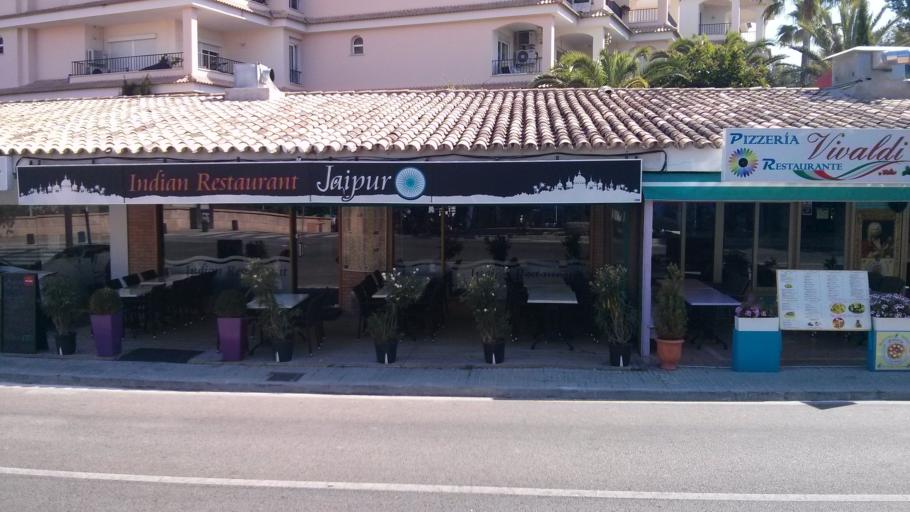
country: ES
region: Balearic Islands
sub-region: Illes Balears
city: Magaluf
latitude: 39.5356
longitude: 2.5708
